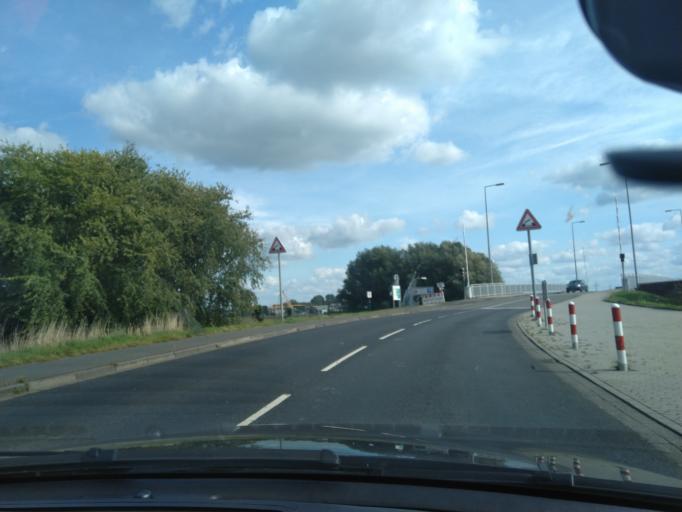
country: DE
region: Lower Saxony
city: Leer
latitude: 53.2155
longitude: 7.4474
